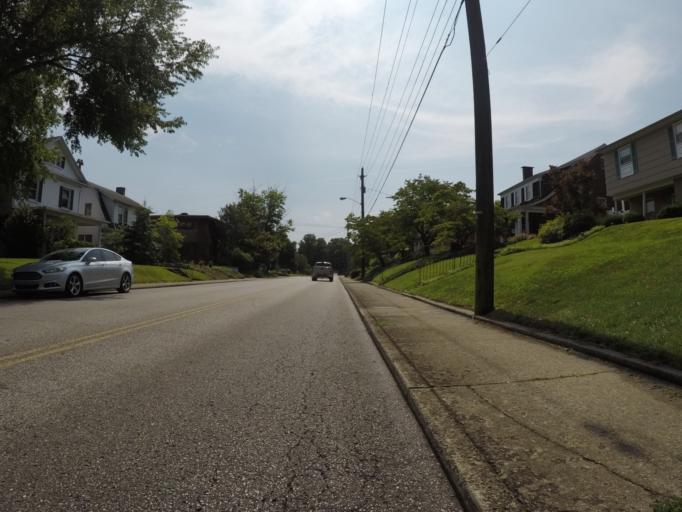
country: US
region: Kentucky
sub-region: Boyd County
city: Ashland
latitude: 38.4750
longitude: -82.6452
